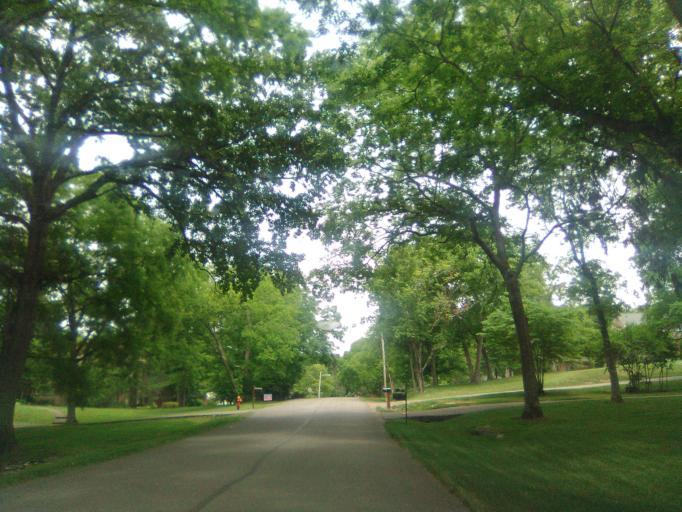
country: US
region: Tennessee
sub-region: Davidson County
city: Belle Meade
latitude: 36.1150
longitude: -86.8804
